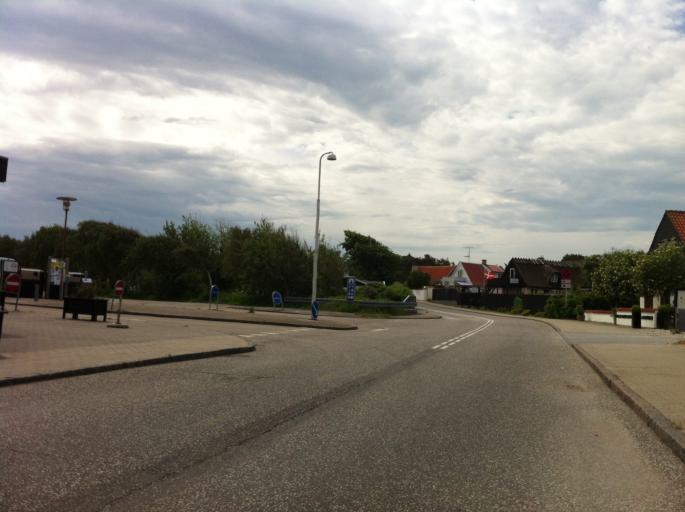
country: DK
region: Capital Region
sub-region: Gribskov Kommune
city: Helsinge
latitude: 56.0981
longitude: 12.1593
